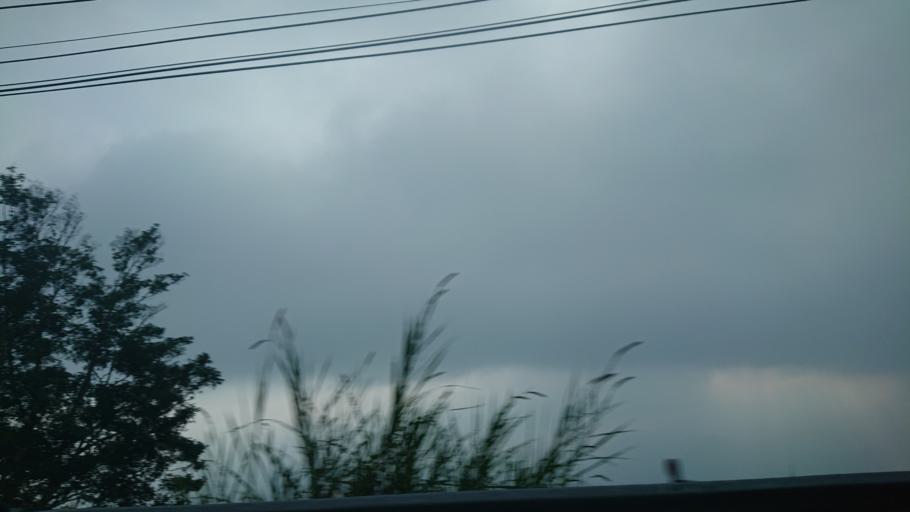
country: TW
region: Taiwan
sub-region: Chiayi
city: Jiayi Shi
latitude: 23.4632
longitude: 120.7192
